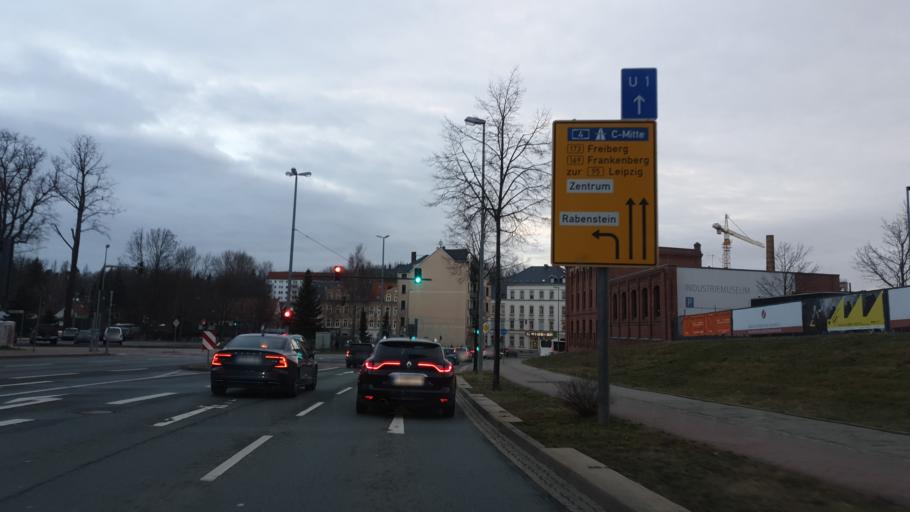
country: DE
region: Saxony
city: Chemnitz
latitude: 50.8231
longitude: 12.8987
